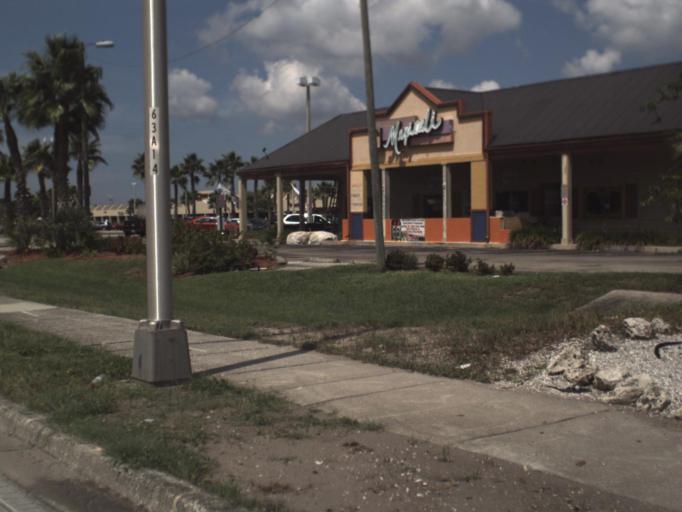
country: US
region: Florida
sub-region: Manatee County
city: South Bradenton
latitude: 27.4627
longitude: -82.6163
